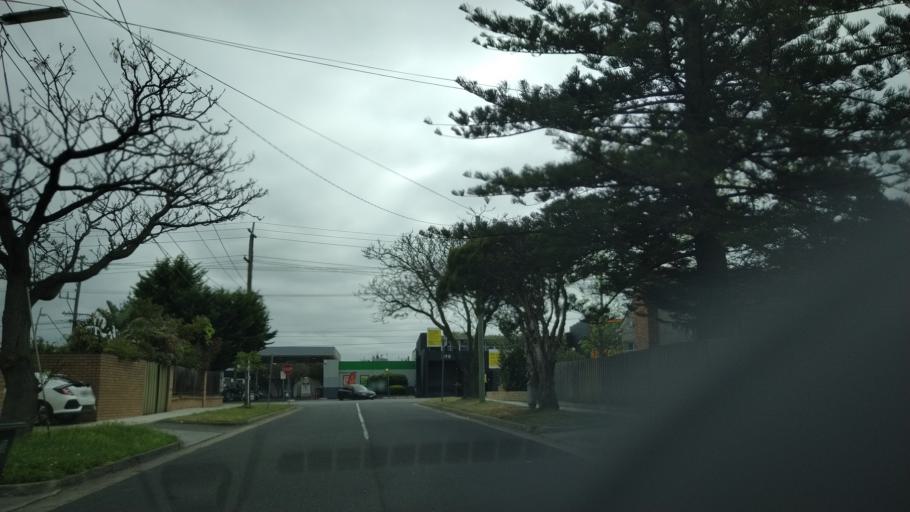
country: AU
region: Victoria
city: Murrumbeena
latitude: -37.9078
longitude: 145.0673
